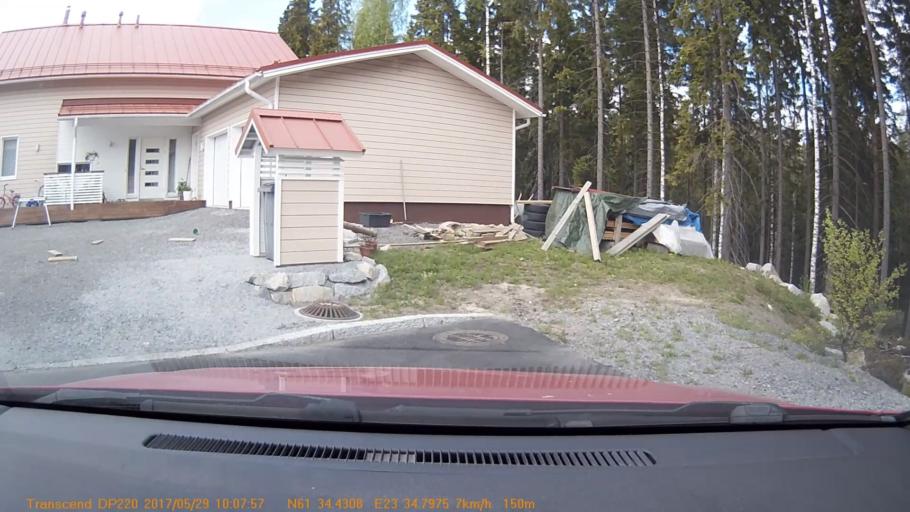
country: FI
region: Pirkanmaa
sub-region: Tampere
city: Yloejaervi
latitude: 61.5738
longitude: 23.5800
